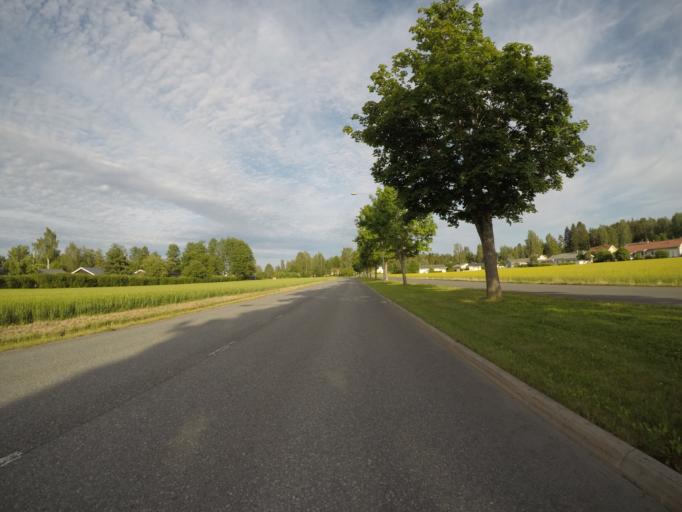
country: FI
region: Haeme
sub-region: Haemeenlinna
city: Haemeenlinna
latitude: 60.9759
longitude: 24.4255
